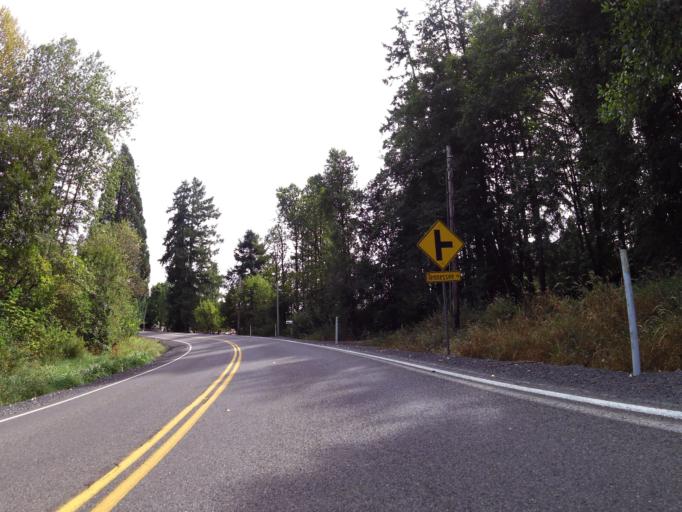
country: US
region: Washington
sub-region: Lewis County
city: Napavine
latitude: 46.5440
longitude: -122.9519
